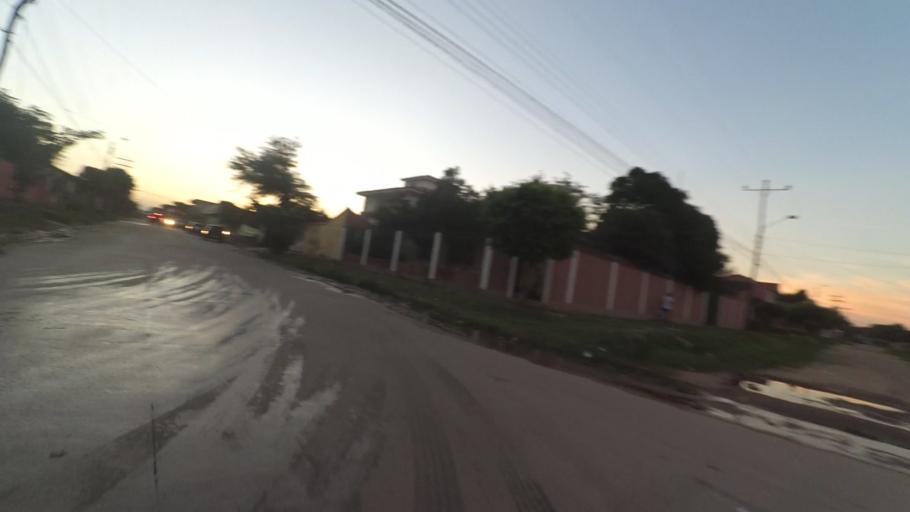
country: BO
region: Santa Cruz
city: Santa Cruz de la Sierra
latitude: -17.8201
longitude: -63.1315
